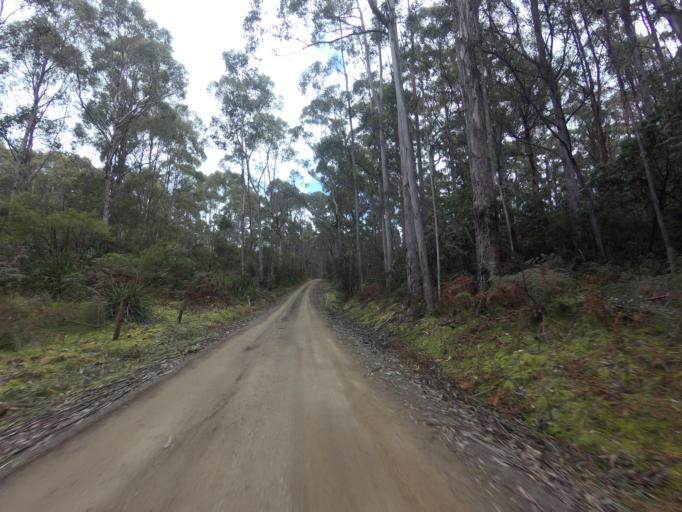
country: AU
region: Tasmania
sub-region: Huon Valley
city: Geeveston
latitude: -43.4233
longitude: 147.0093
